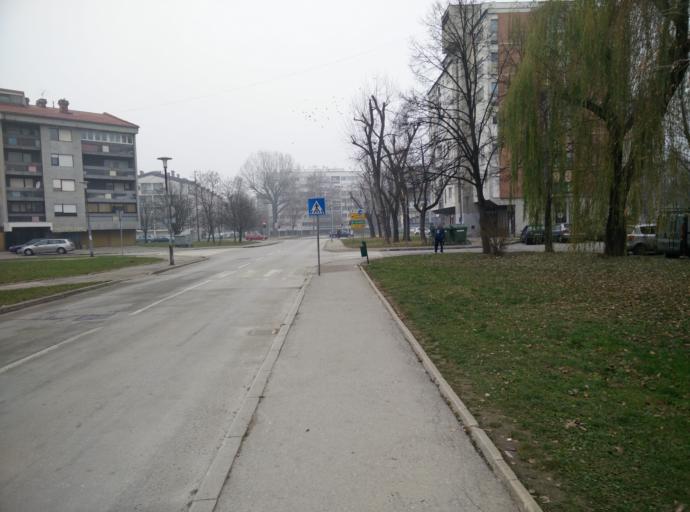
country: HR
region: Karlovacka
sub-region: Grad Karlovac
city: Karlovac
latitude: 45.4852
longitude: 15.5492
